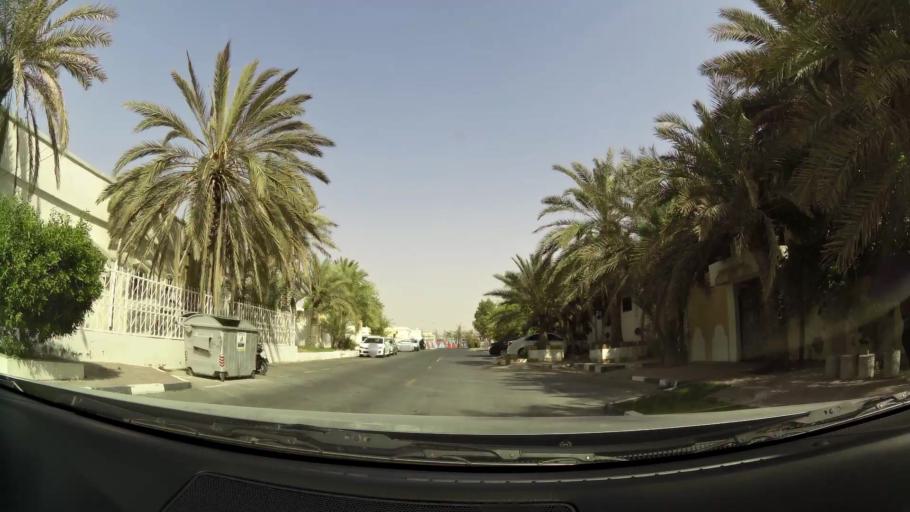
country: AE
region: Dubai
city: Dubai
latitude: 25.1701
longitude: 55.2445
